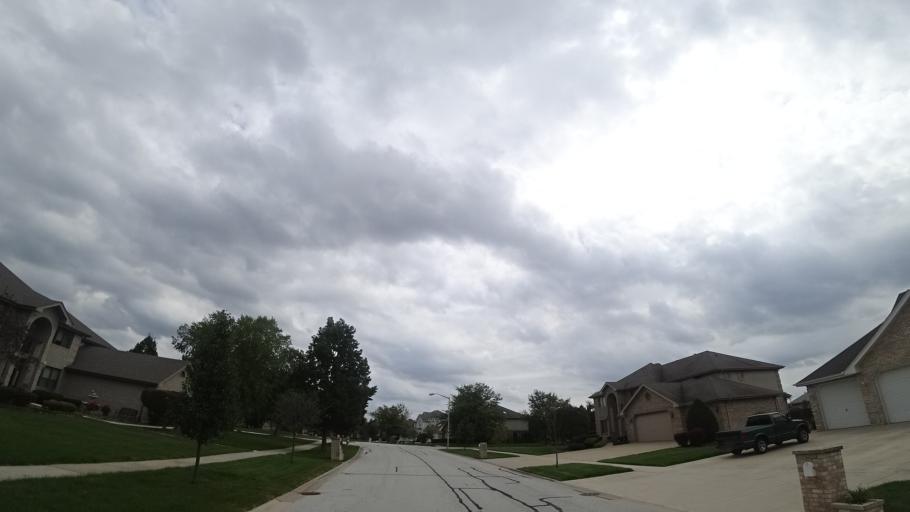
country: US
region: Illinois
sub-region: Cook County
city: Tinley Park
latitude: 41.5687
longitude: -87.8114
